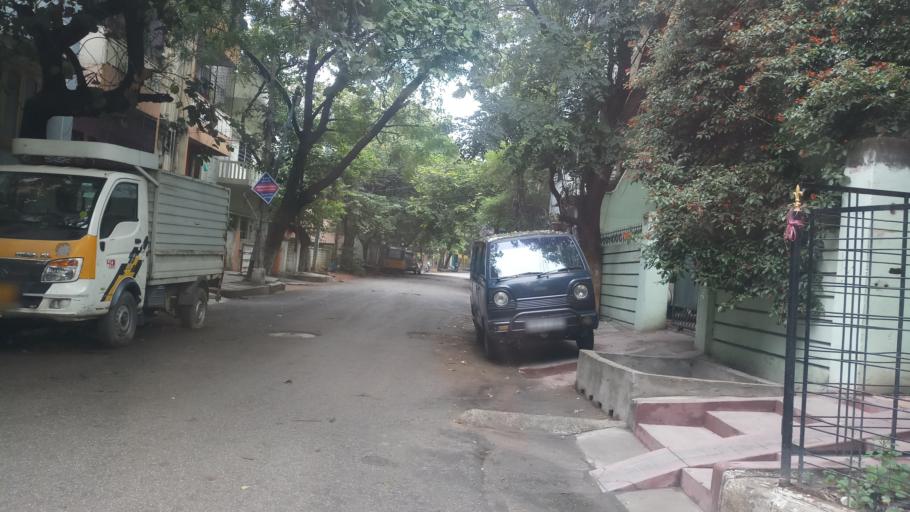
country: IN
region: Telangana
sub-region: Hyderabad
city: Hyderabad
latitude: 17.3936
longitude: 78.4529
